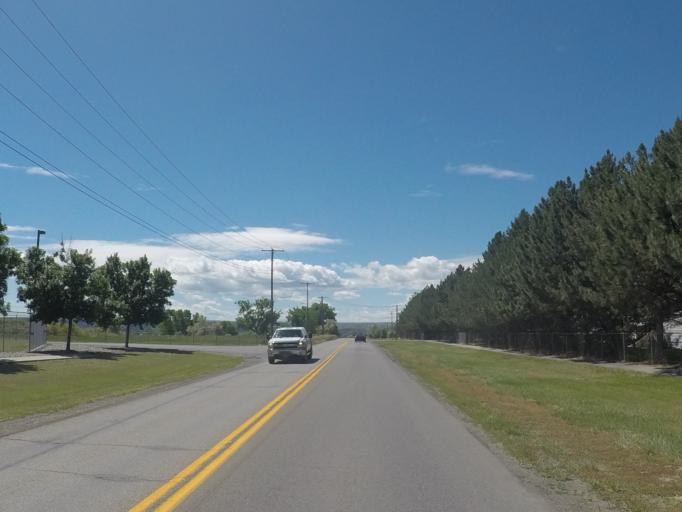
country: US
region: Montana
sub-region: Yellowstone County
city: Billings
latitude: 45.7505
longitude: -108.5969
